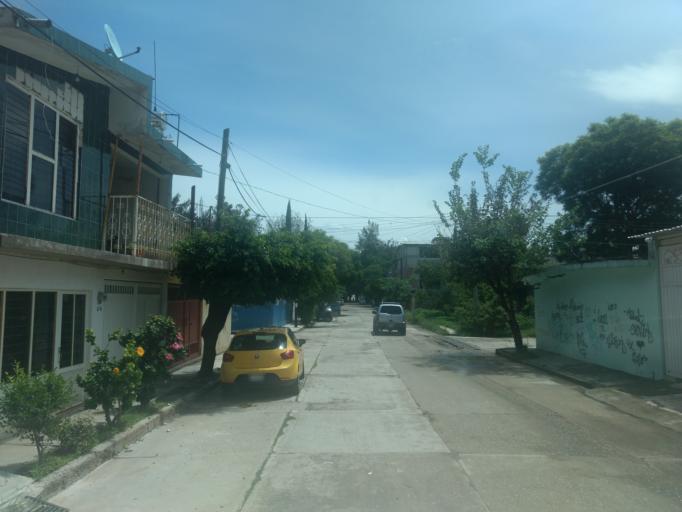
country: MX
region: Oaxaca
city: Ciudad de Huajuapam de Leon
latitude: 17.7997
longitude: -97.7784
